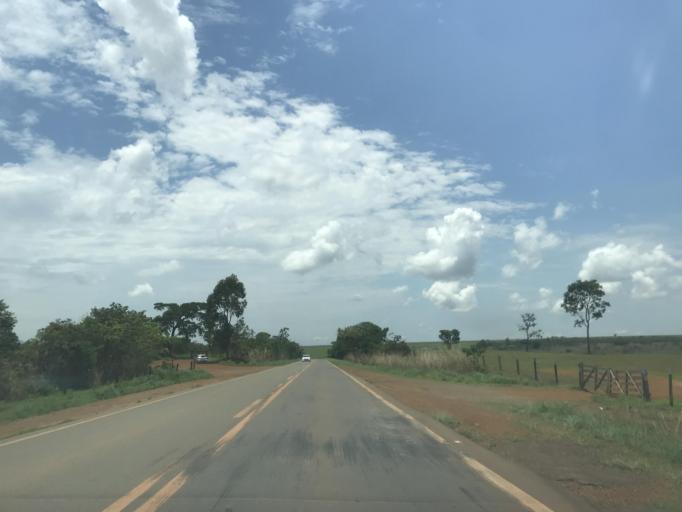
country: BR
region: Goias
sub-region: Luziania
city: Luziania
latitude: -16.4779
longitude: -48.2075
